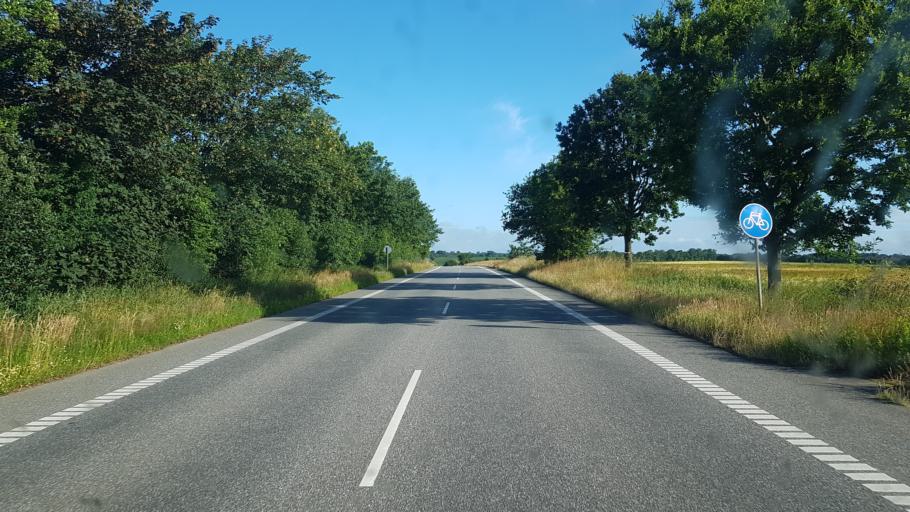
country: DK
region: South Denmark
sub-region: Vejen Kommune
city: Rodding
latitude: 55.3828
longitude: 9.0515
